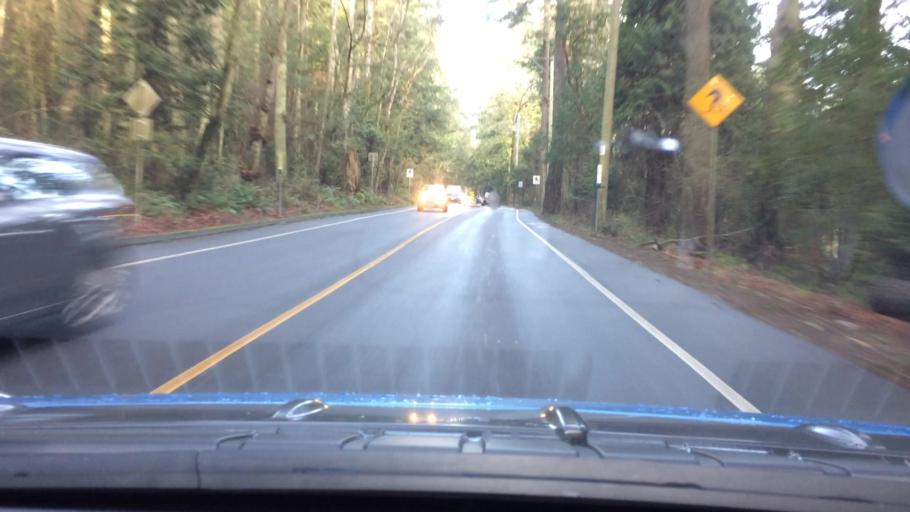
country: CA
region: British Columbia
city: Oak Bay
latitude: 48.4956
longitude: -123.3358
